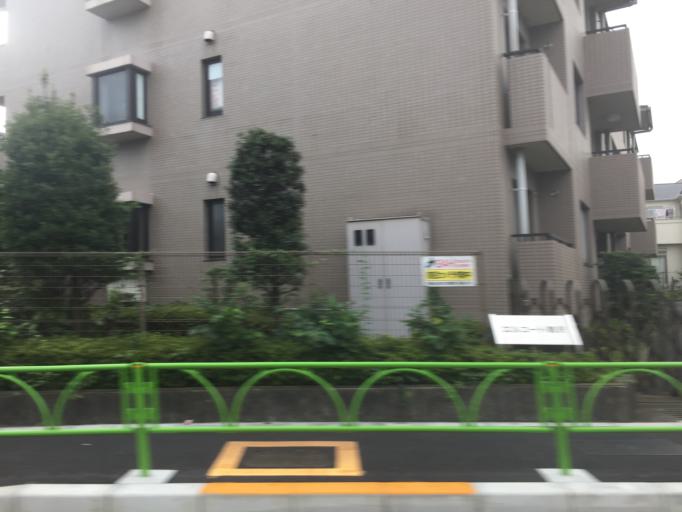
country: JP
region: Tokyo
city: Tokyo
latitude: 35.6348
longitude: 139.6545
